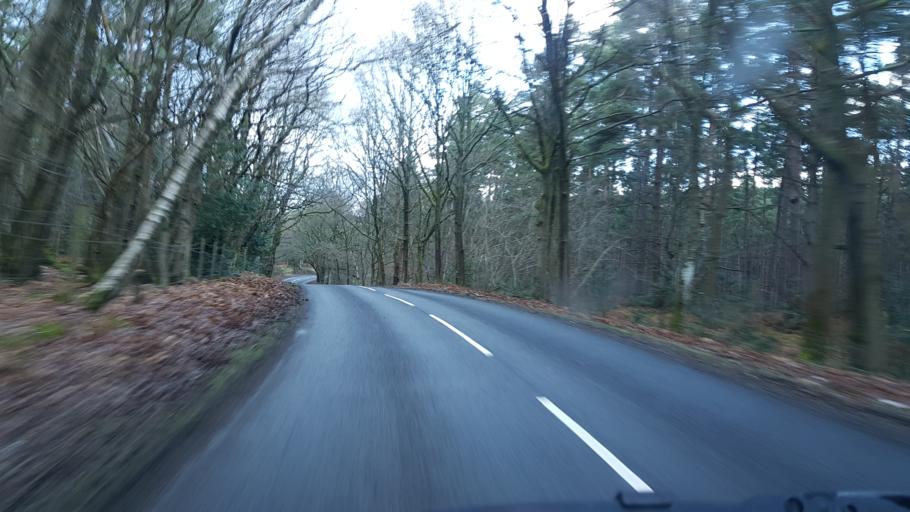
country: GB
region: England
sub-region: Surrey
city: Elstead
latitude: 51.1975
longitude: -0.7171
